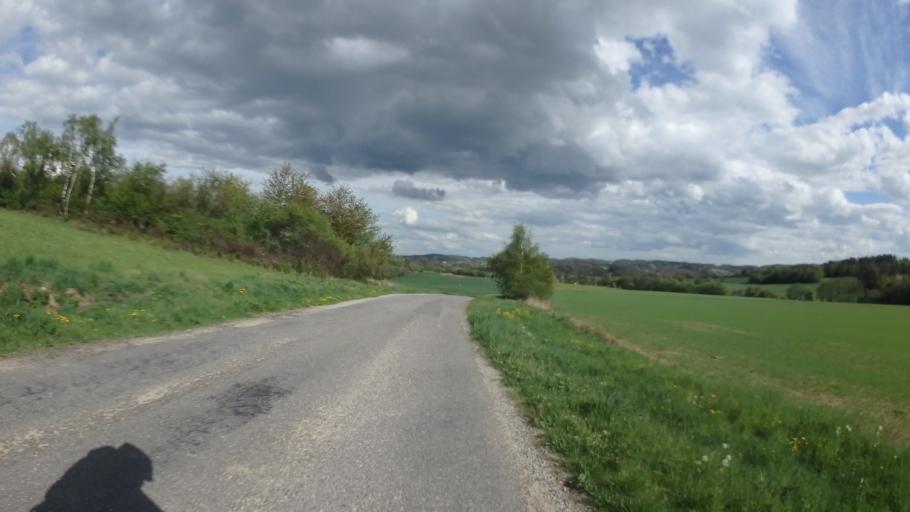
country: CZ
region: Vysocina
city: Merin
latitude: 49.3435
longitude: 15.8880
